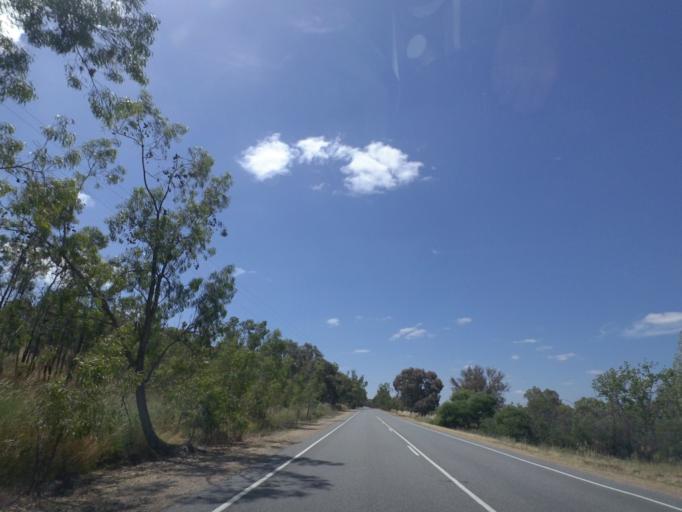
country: AU
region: Victoria
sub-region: Wangaratta
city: Wangaratta
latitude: -36.4561
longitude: 146.2368
